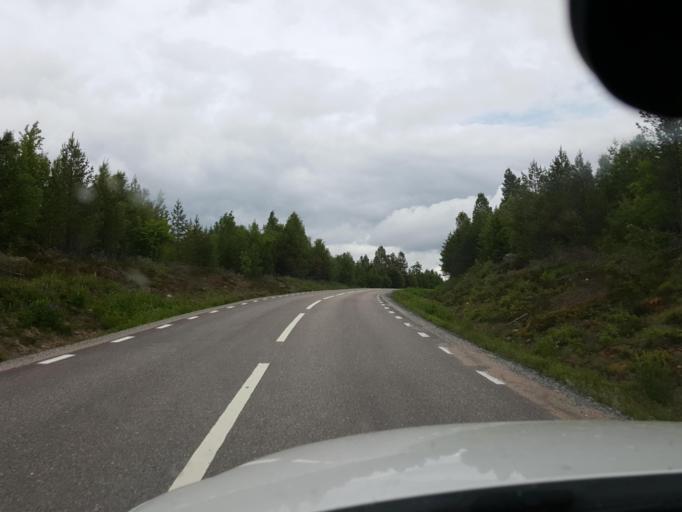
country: SE
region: Gaevleborg
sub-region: Ljusdals Kommun
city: Farila
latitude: 61.7553
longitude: 15.3783
